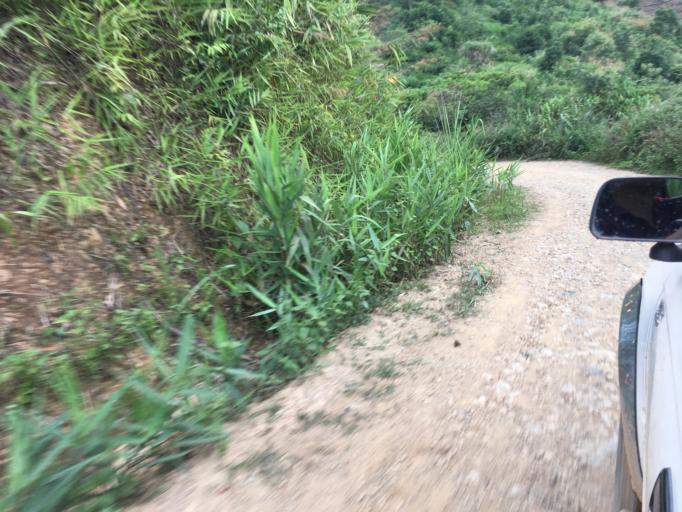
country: LA
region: Oudomxai
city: Muang La
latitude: 20.8846
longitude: 102.3450
